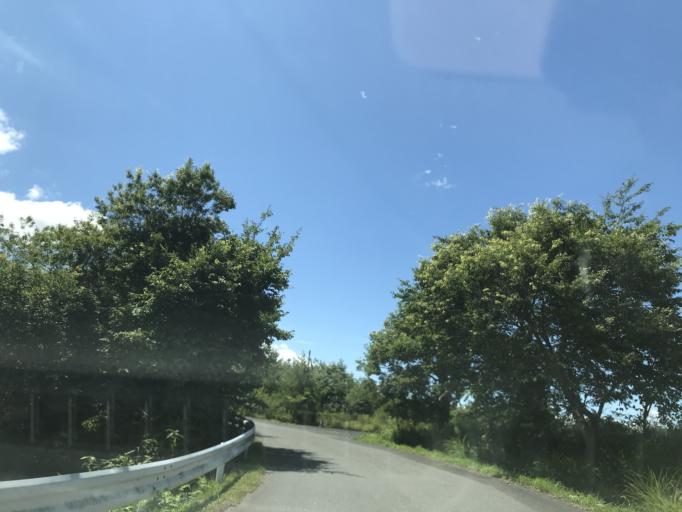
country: JP
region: Iwate
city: Ichinoseki
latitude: 38.9308
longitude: 141.0374
